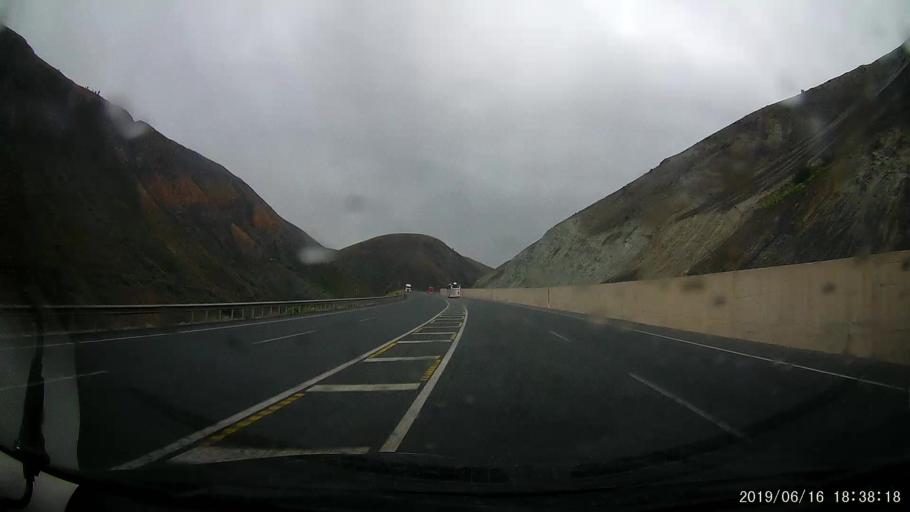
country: TR
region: Erzincan
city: Catalarmut
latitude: 39.8847
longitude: 39.1835
